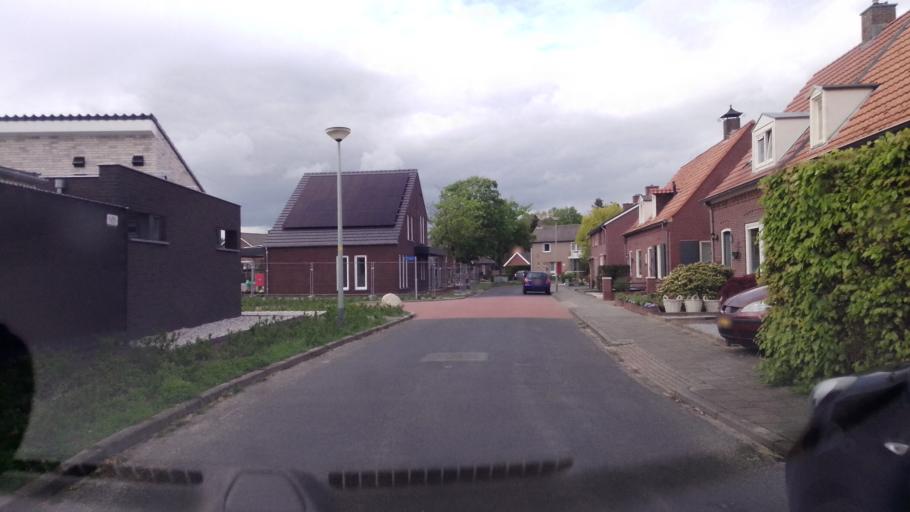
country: NL
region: Limburg
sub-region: Gemeente Venlo
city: Arcen
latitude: 51.4622
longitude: 6.1591
